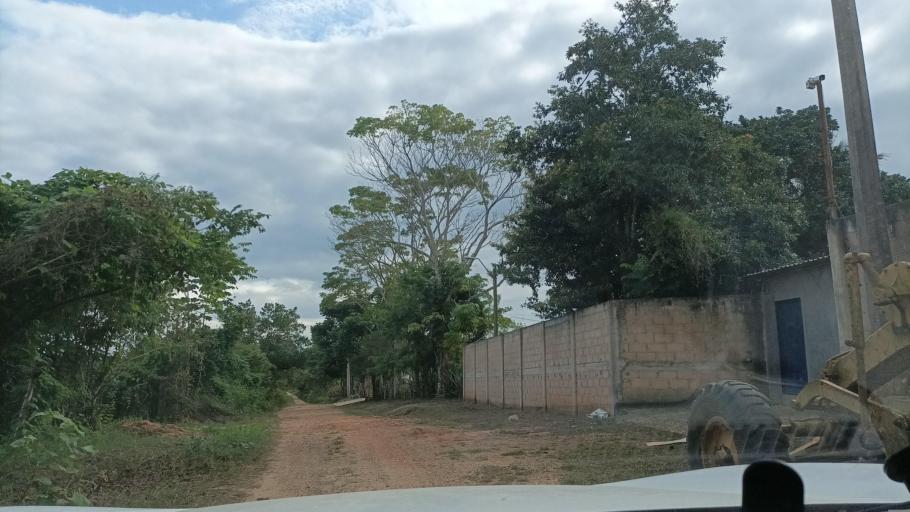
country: MX
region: Veracruz
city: Oluta
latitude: 17.9415
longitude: -94.8822
